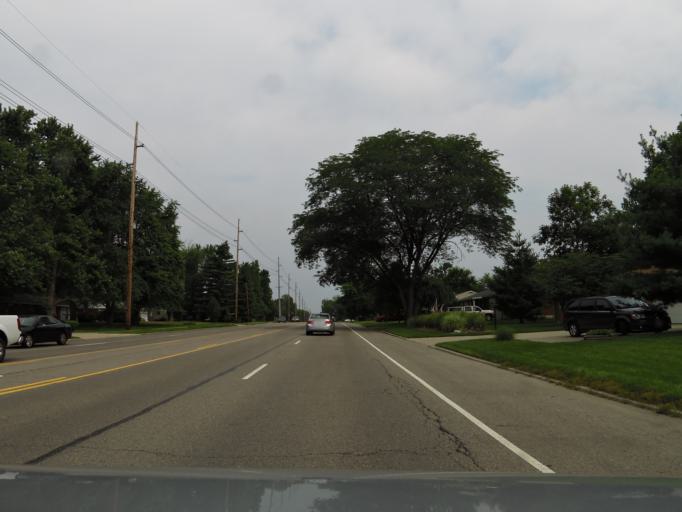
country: US
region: Ohio
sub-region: Greene County
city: Bellbrook
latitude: 39.6690
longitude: -84.1099
